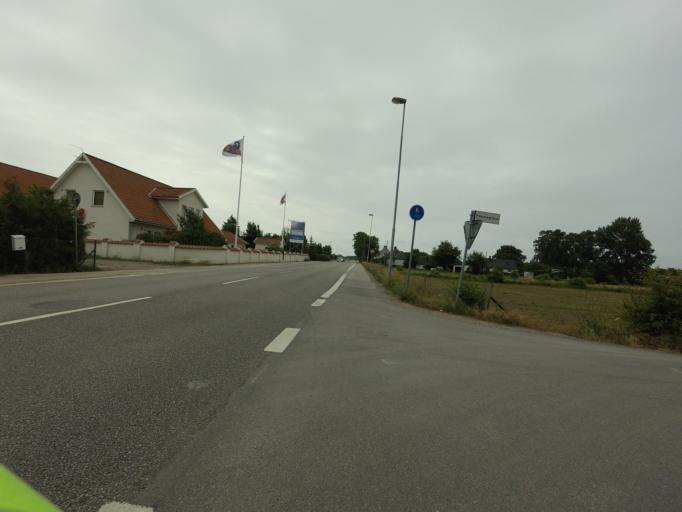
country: SE
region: Skane
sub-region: Malmo
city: Bunkeflostrand
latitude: 55.5464
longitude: 12.9181
